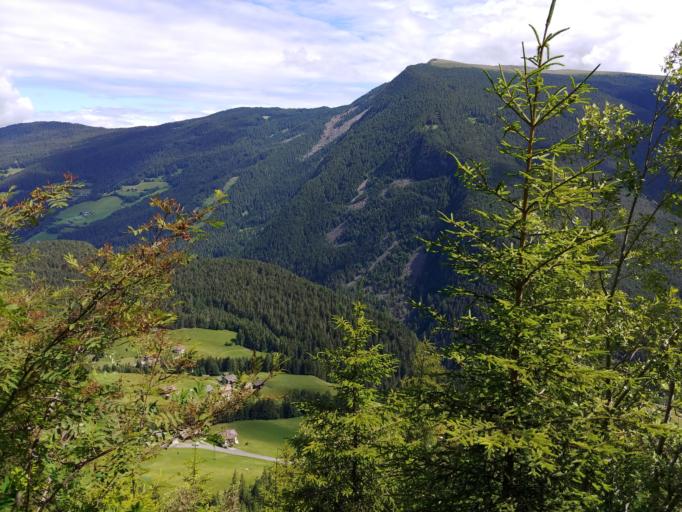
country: IT
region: Trentino-Alto Adige
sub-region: Bolzano
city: Ortisei
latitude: 46.5690
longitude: 11.6325
